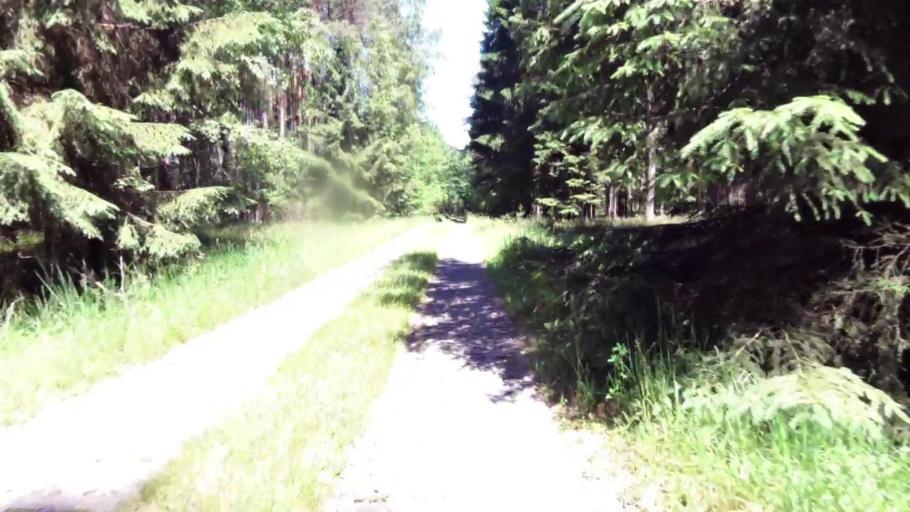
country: PL
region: West Pomeranian Voivodeship
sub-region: Powiat bialogardzki
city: Tychowo
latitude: 53.9299
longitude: 16.1209
